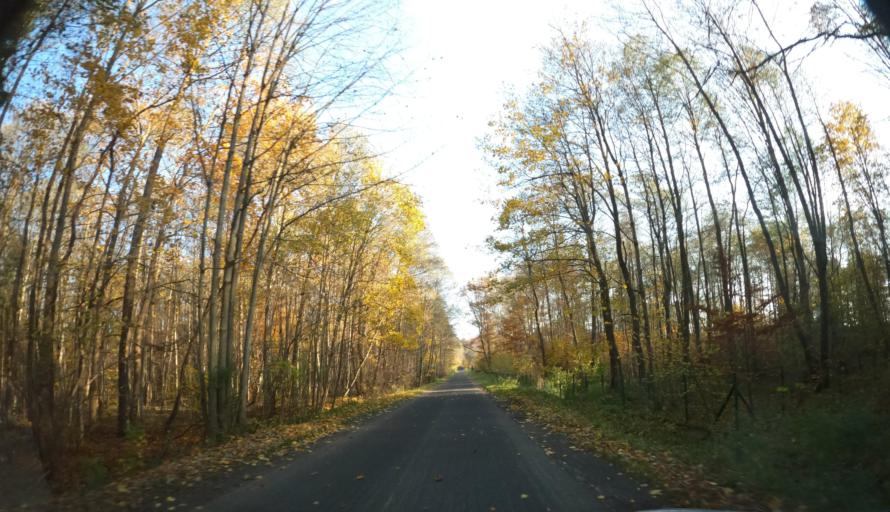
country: PL
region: West Pomeranian Voivodeship
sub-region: Powiat koszalinski
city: Polanow
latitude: 54.2404
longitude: 16.7214
